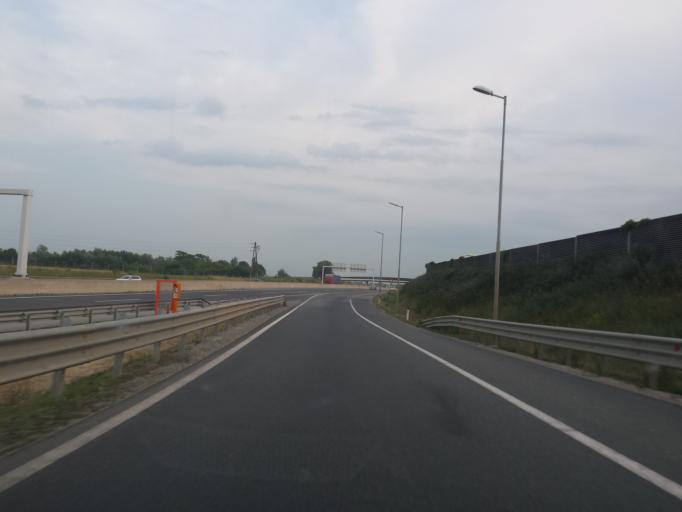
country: AT
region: Lower Austria
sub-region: Politischer Bezirk Ganserndorf
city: Aderklaa
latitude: 48.2805
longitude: 16.5108
